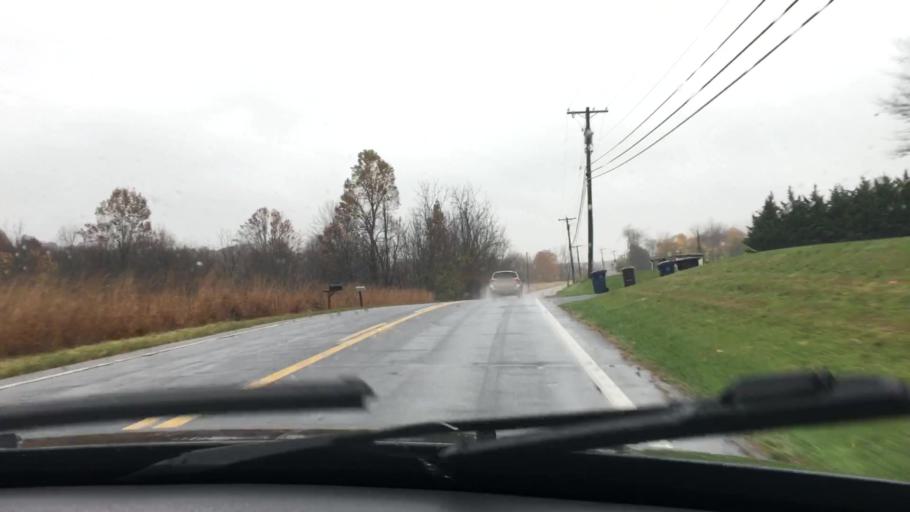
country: US
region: Maryland
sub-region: Carroll County
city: Manchester
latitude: 39.6851
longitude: -76.8830
